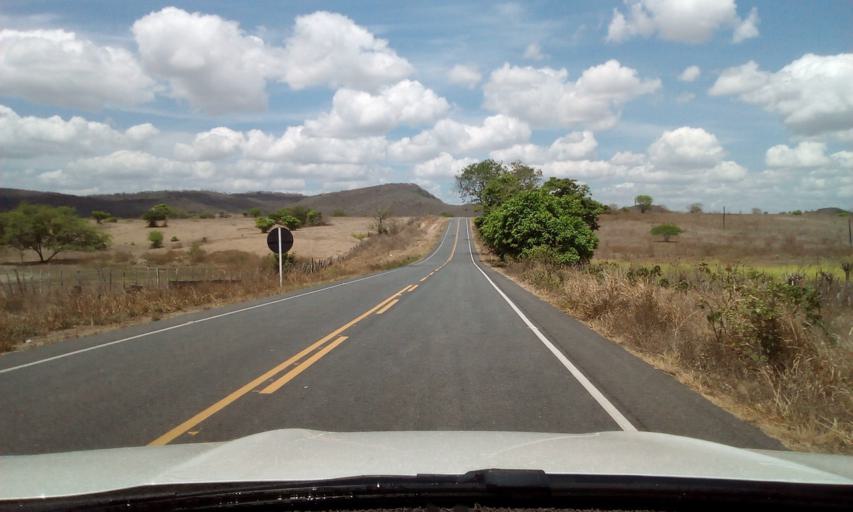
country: BR
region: Paraiba
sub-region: Gurinhem
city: Gurinhem
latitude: -7.1565
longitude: -35.3900
